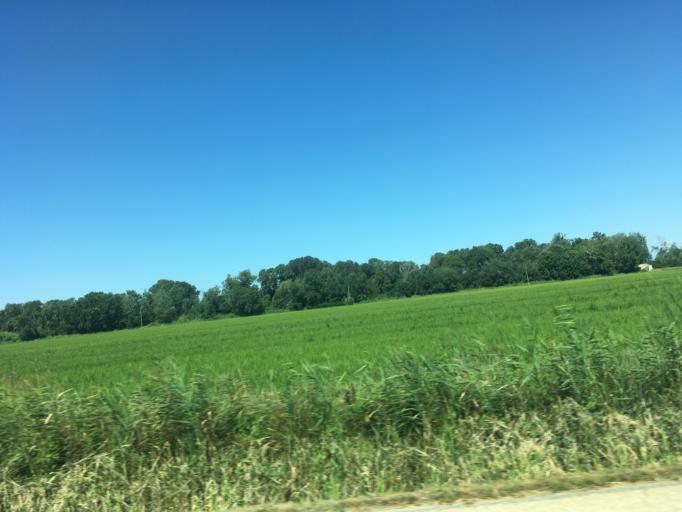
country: FR
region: Languedoc-Roussillon
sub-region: Departement du Gard
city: Saint-Gilles
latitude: 43.5958
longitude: 4.4707
